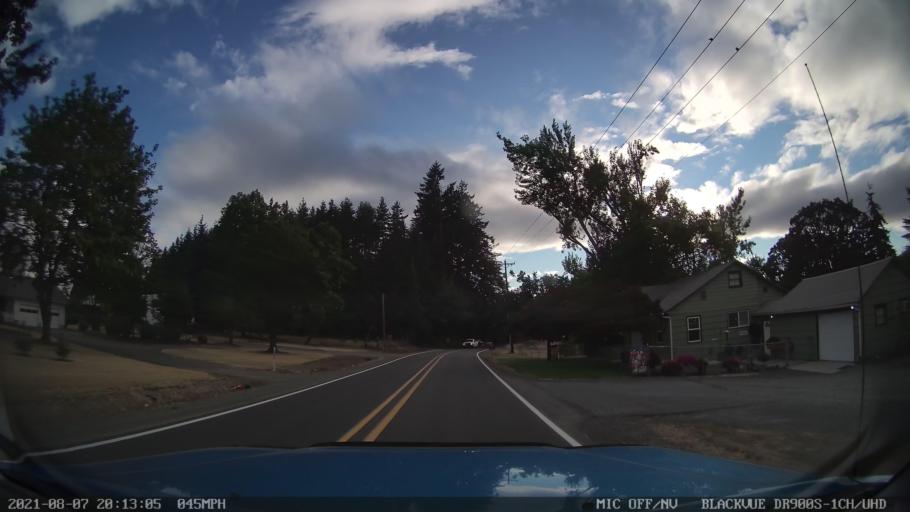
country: US
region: Oregon
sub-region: Marion County
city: Hayesville
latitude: 44.9565
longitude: -122.9187
